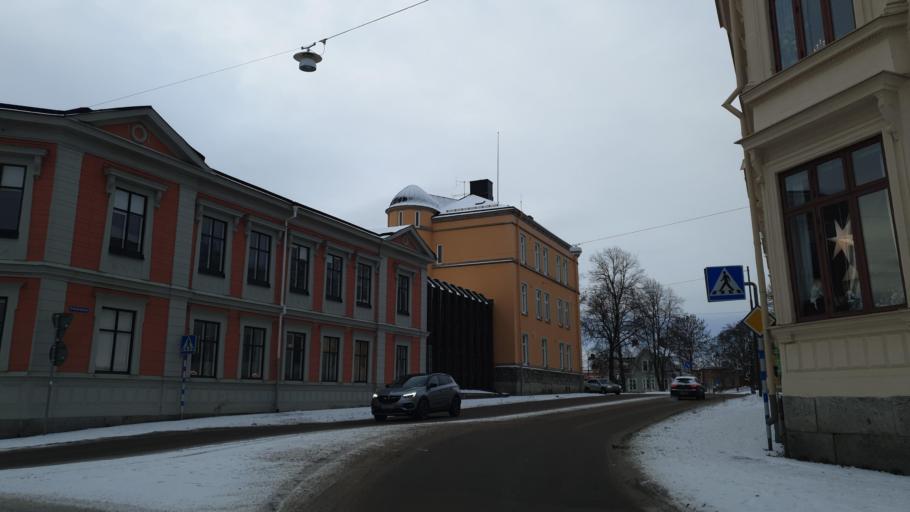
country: SE
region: Gaevleborg
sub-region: Soderhamns Kommun
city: Soderhamn
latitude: 61.3015
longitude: 17.0527
